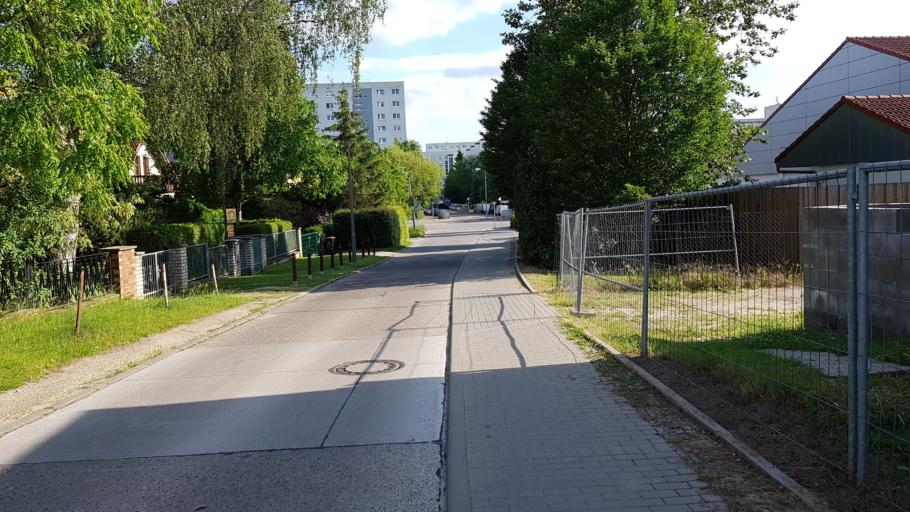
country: DE
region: Berlin
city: Marzahn
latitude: 52.5295
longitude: 13.5717
